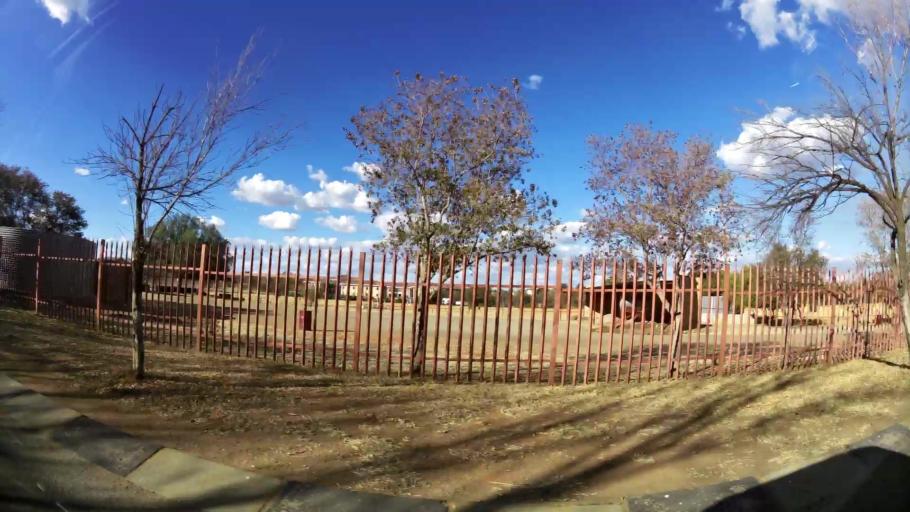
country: ZA
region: North-West
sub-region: Dr Kenneth Kaunda District Municipality
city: Klerksdorp
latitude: -26.8408
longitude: 26.6627
